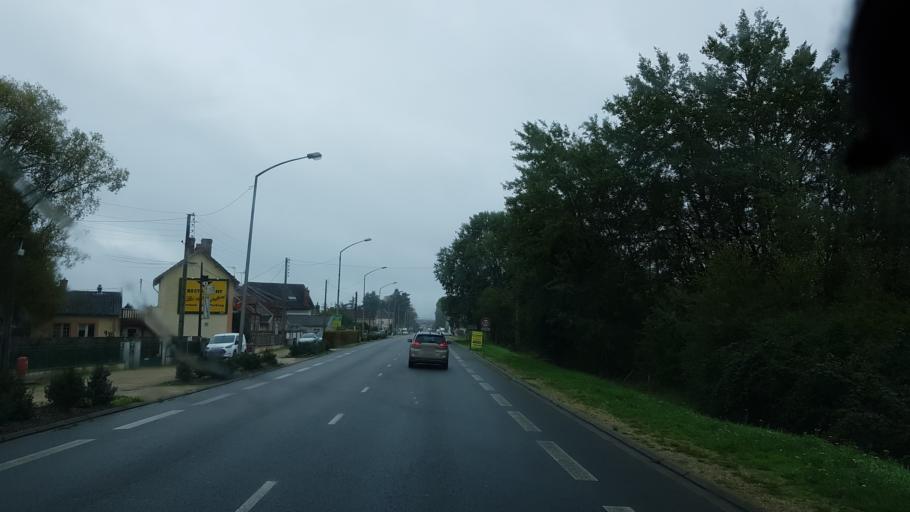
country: FR
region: Centre
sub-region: Departement du Loir-et-Cher
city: Salbris
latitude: 47.4351
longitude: 2.0490
